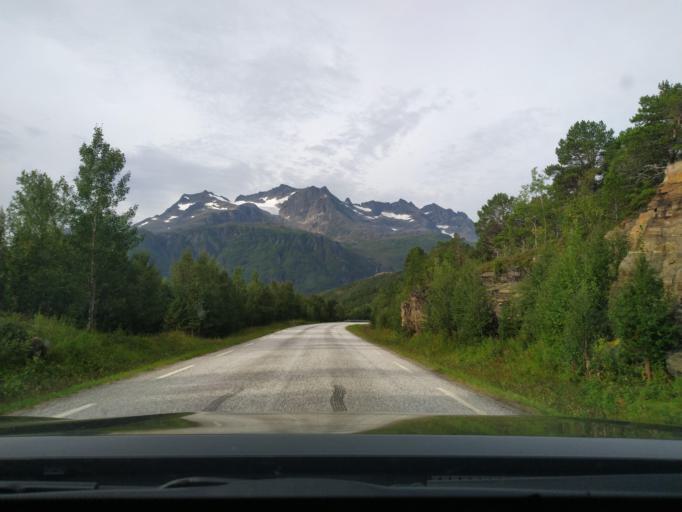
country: NO
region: Troms
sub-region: Dyroy
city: Brostadbotn
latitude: 68.9036
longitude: 17.4906
